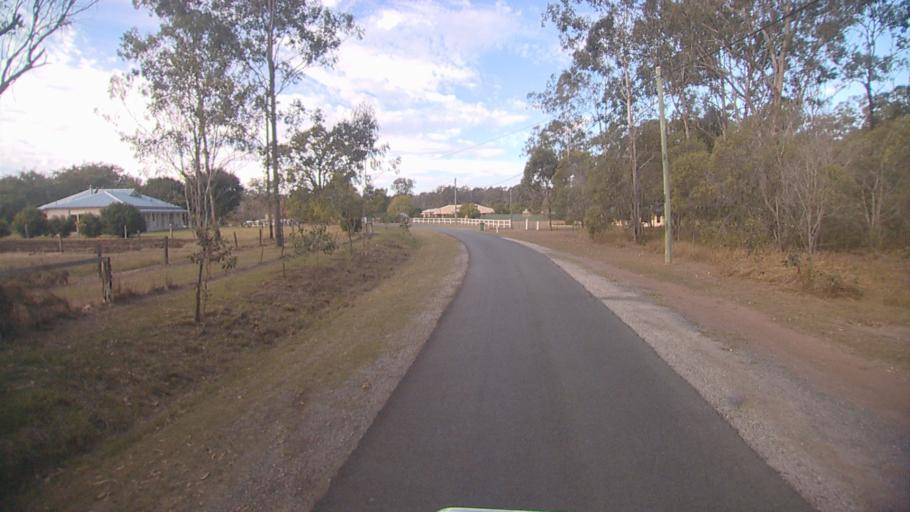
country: AU
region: Queensland
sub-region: Logan
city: North Maclean
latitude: -27.7542
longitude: 152.9815
